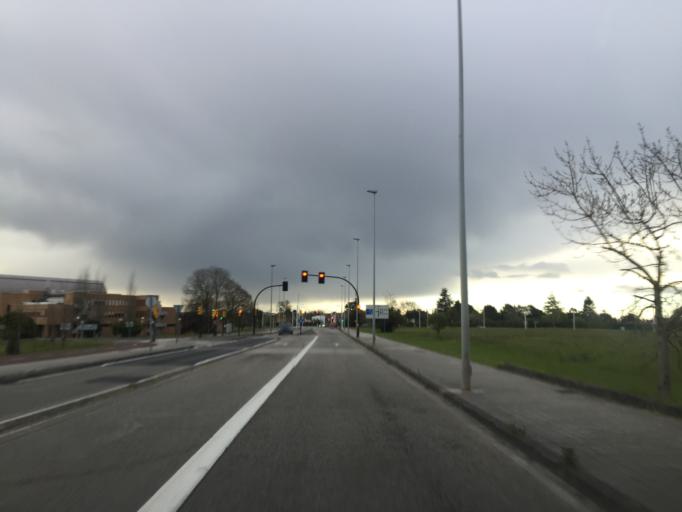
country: ES
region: Asturias
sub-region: Province of Asturias
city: Gijon
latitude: 43.5259
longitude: -5.6260
